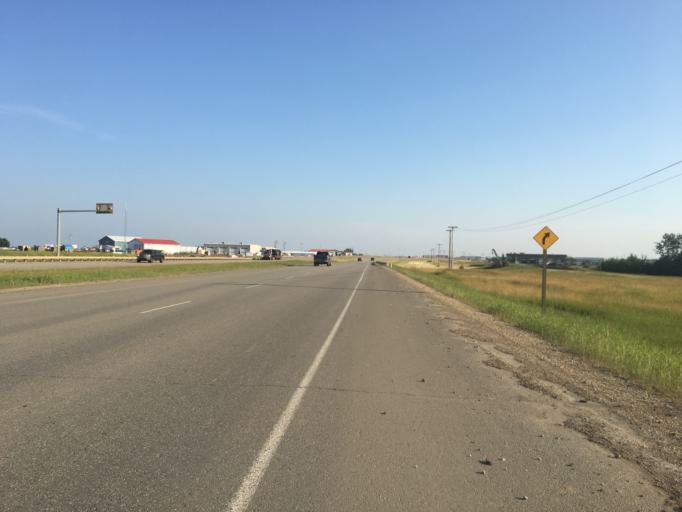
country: CA
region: Alberta
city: Sexsmith
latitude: 55.2726
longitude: -118.7951
